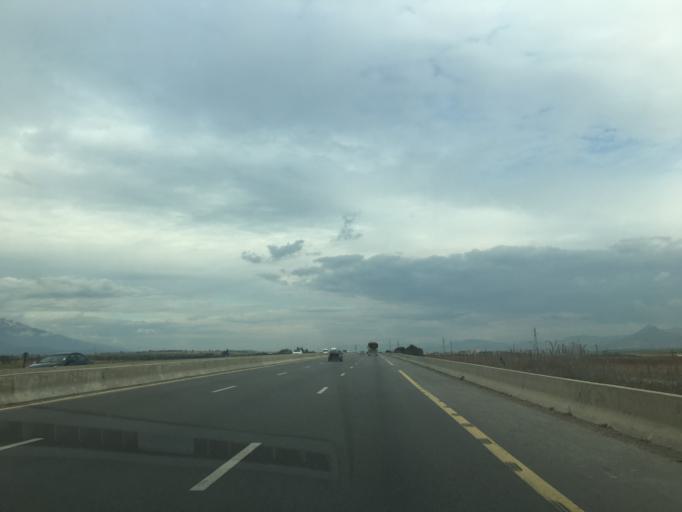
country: DZ
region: Bouira
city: Bouira
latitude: 36.3276
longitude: 3.9720
